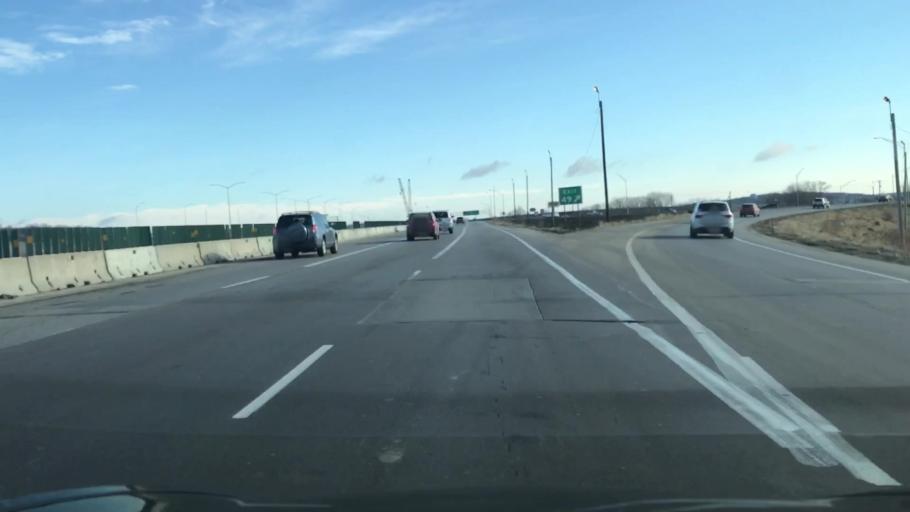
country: US
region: Iowa
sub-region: Pottawattamie County
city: Council Bluffs
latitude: 41.2314
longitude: -95.8549
